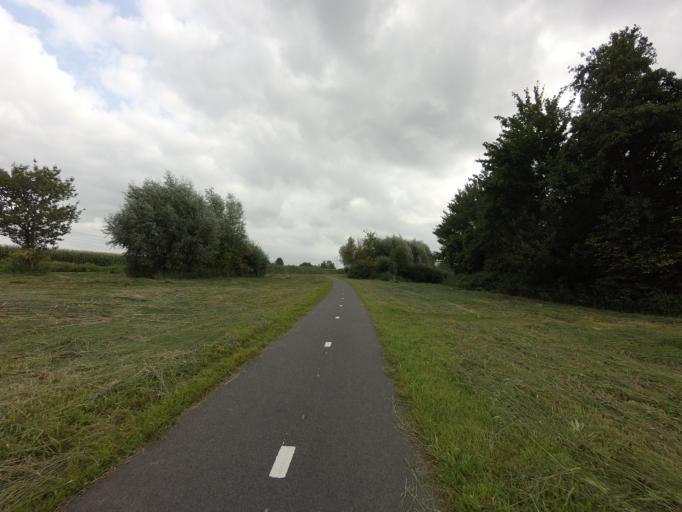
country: NL
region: North Holland
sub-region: Gemeente Diemen
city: Diemen
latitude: 52.3871
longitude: 4.9746
